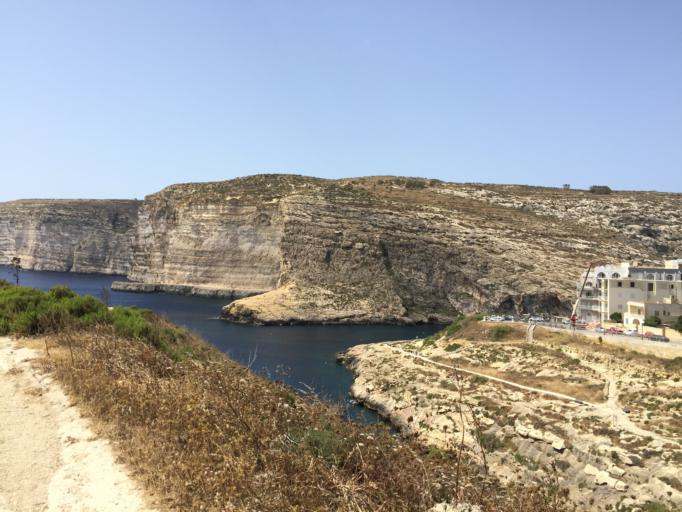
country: MT
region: Saint Lucia
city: Saint Lucia
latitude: 36.0270
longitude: 14.2164
